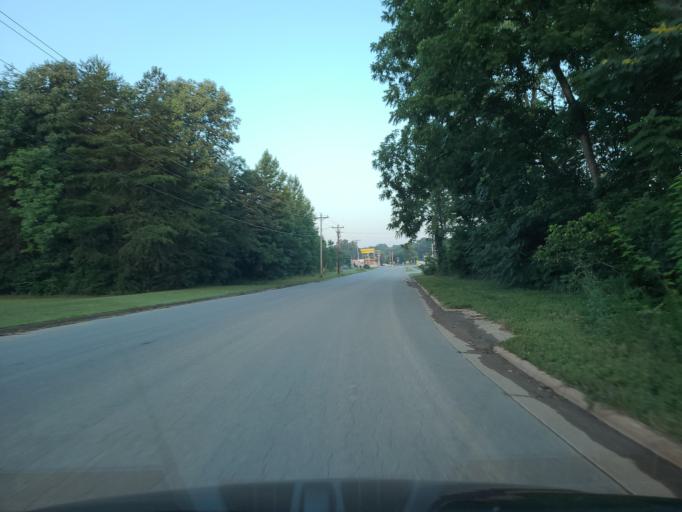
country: US
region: North Carolina
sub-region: Iredell County
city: Statesville
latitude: 35.8059
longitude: -80.8723
